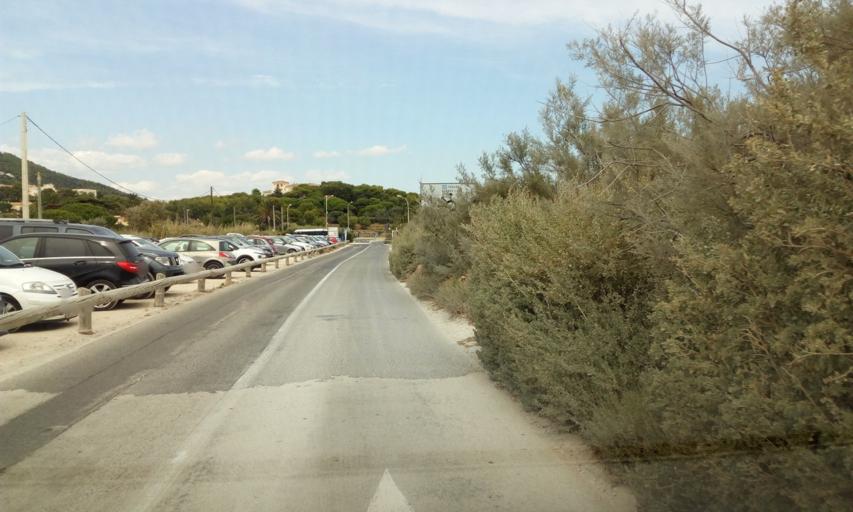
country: FR
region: Provence-Alpes-Cote d'Azur
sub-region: Departement du Var
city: Hyeres
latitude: 43.0781
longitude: 6.1266
